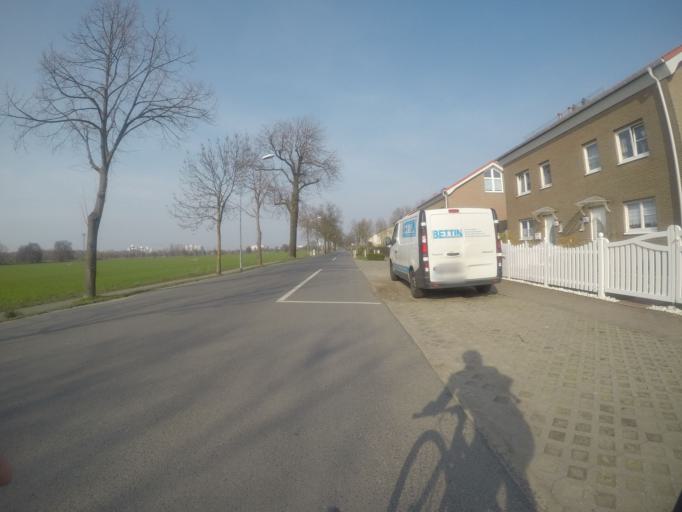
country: DE
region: Brandenburg
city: Schonefeld
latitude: 52.3754
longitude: 13.4683
